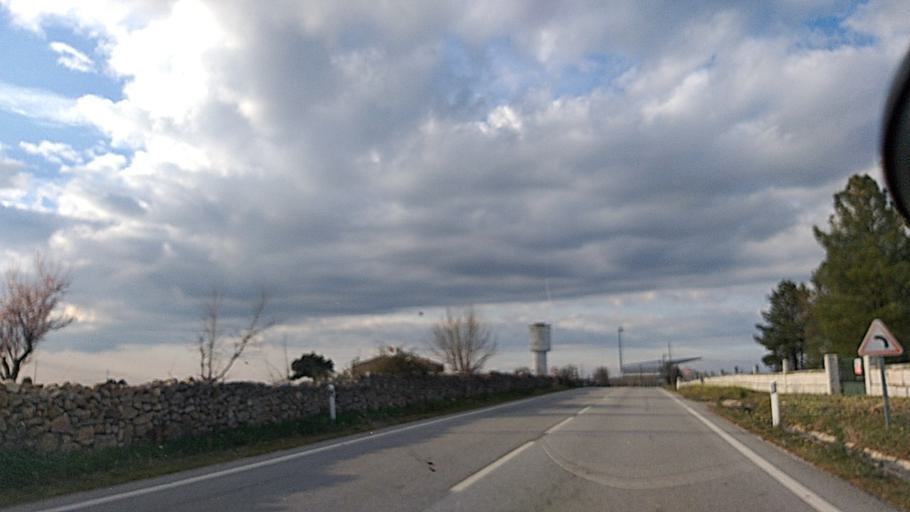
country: ES
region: Castille and Leon
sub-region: Provincia de Salamanca
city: Aldea del Obispo
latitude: 40.7104
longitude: -6.8979
